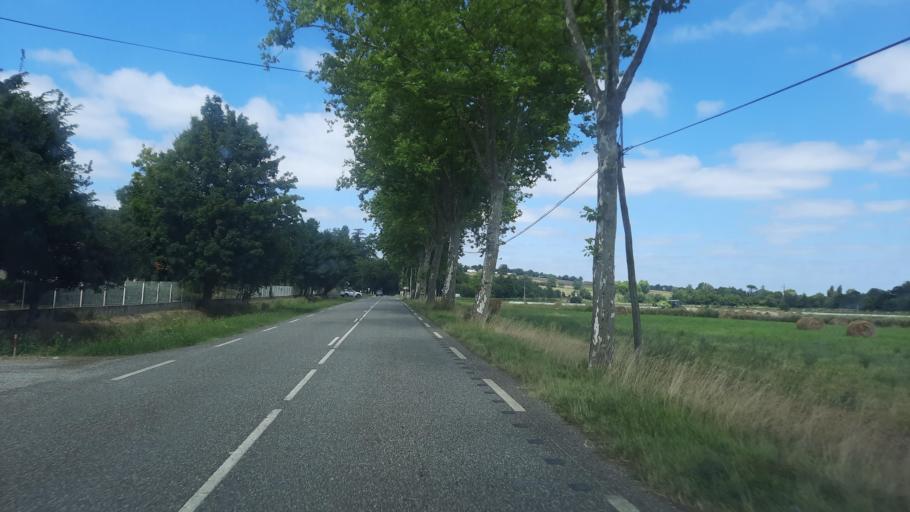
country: FR
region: Midi-Pyrenees
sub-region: Departement de la Haute-Garonne
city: Boulogne-sur-Gesse
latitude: 43.3744
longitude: 0.7547
